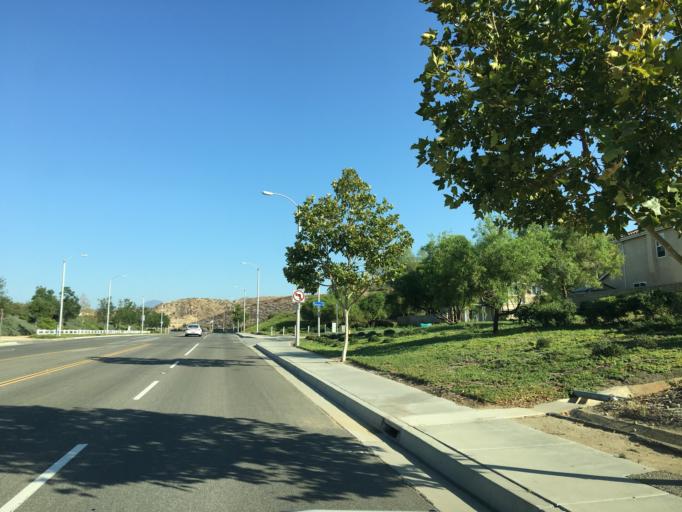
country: US
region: California
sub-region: Los Angeles County
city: Val Verde
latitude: 34.4546
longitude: -118.6333
